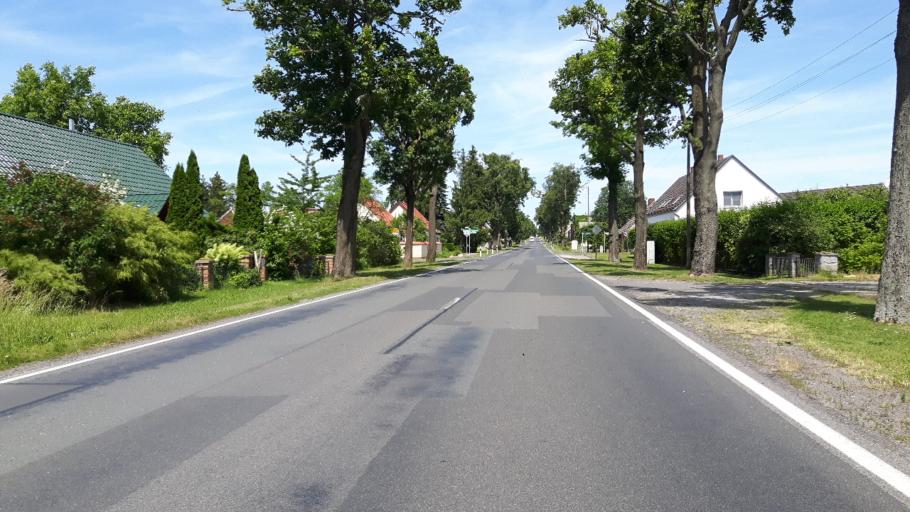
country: DE
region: Saxony-Anhalt
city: Kropstadt
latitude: 52.0336
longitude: 12.8042
